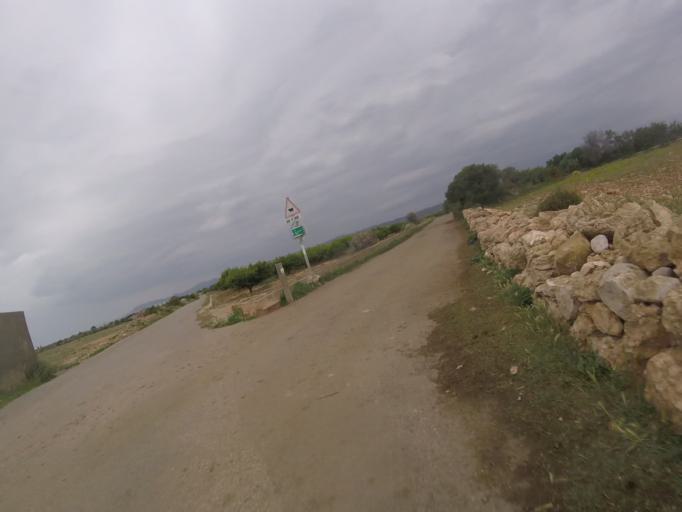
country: ES
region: Valencia
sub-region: Provincia de Castello
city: Torreblanca
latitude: 40.2129
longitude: 0.2445
